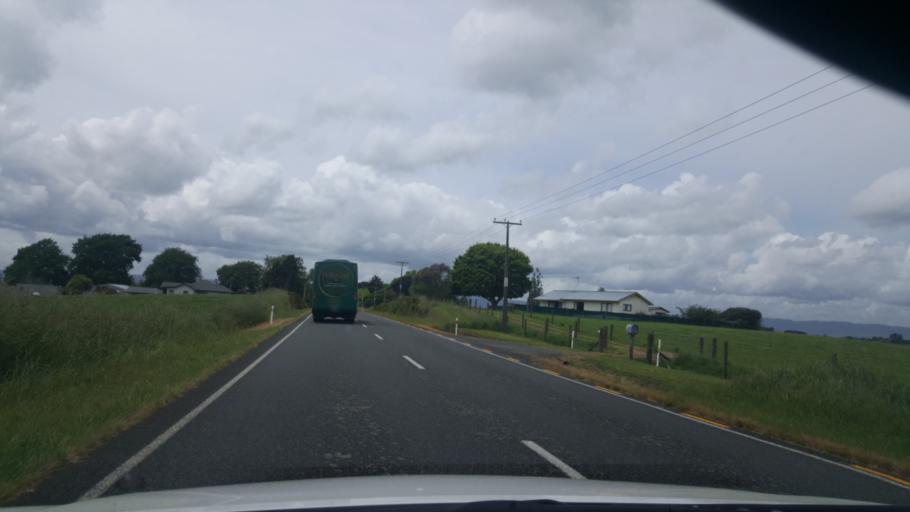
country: NZ
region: Waikato
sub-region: Matamata-Piako District
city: Matamata
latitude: -37.8765
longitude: 175.7194
